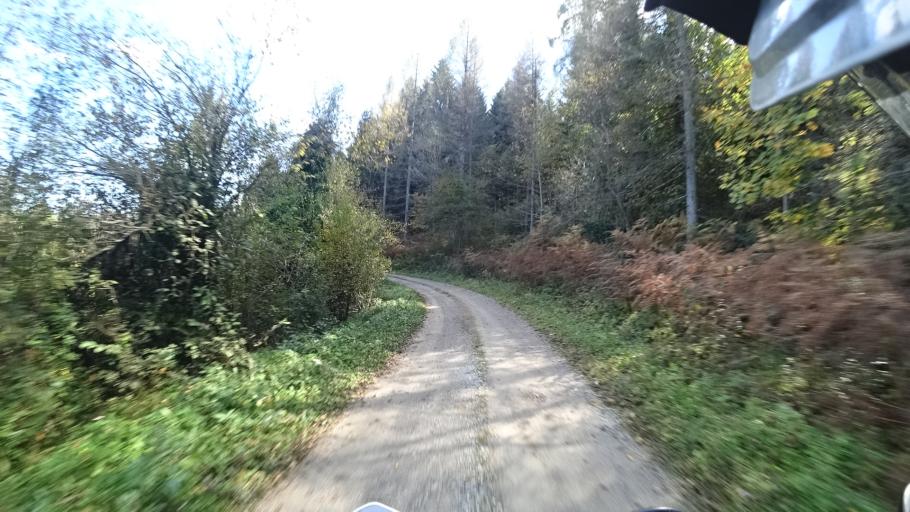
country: HR
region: Karlovacka
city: Plaski
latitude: 45.0733
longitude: 15.3486
